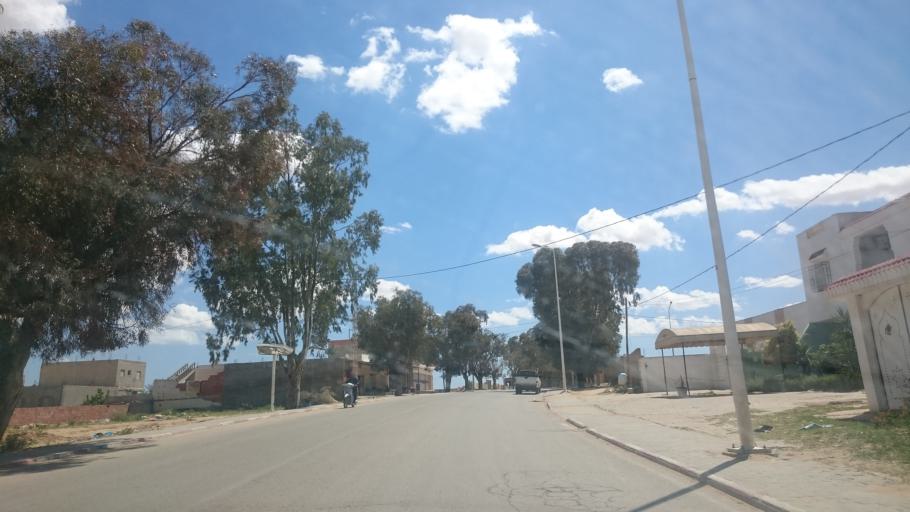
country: TN
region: Safaqis
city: Sfax
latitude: 34.7338
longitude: 10.5329
